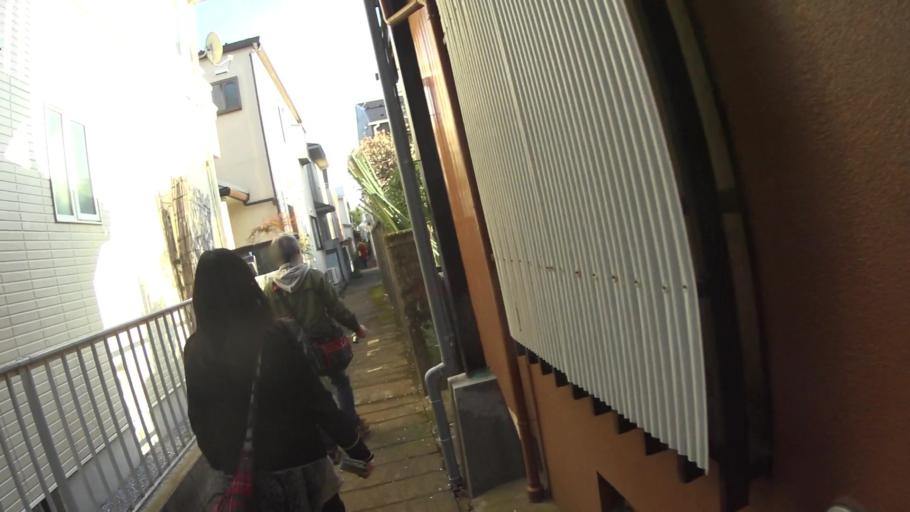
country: JP
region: Tokyo
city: Mitaka-shi
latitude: 35.6455
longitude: 139.6100
